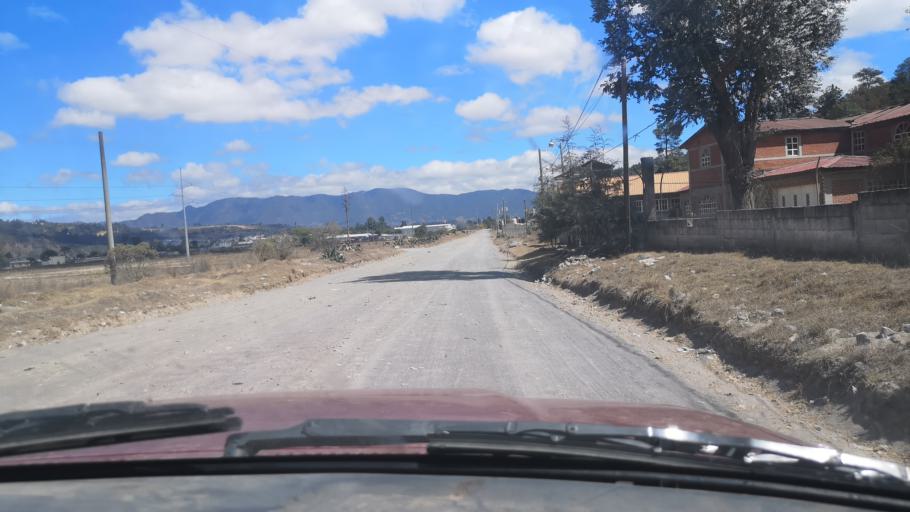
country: GT
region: Quetzaltenango
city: Quetzaltenango
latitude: 14.8106
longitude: -91.5360
